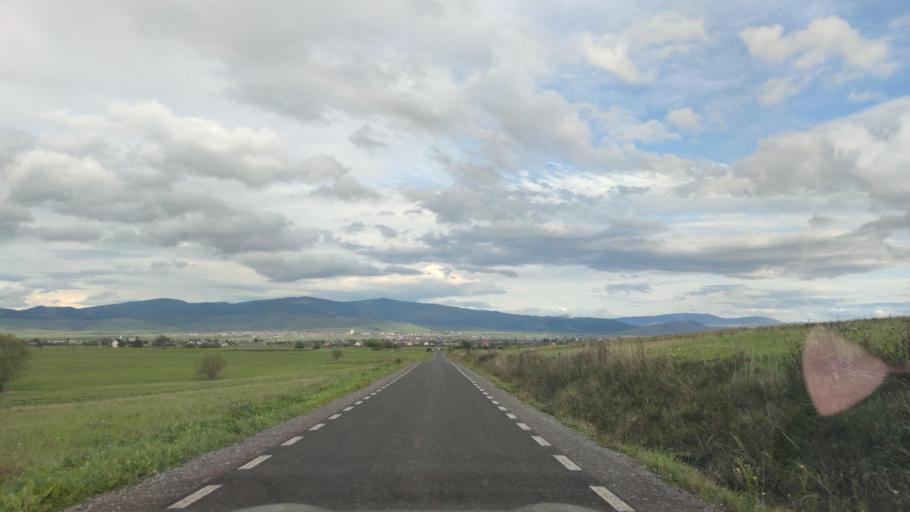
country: RO
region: Harghita
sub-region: Comuna Remetea
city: Remetea
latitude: 46.8060
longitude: 25.4250
